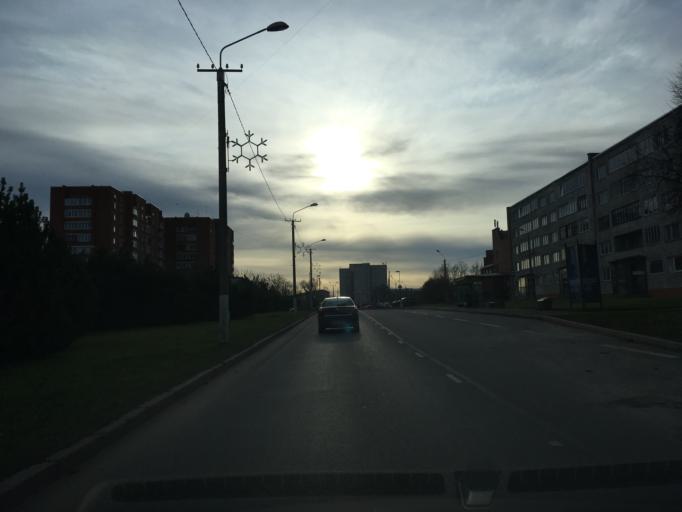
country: EE
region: Ida-Virumaa
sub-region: Narva linn
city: Narva
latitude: 59.3820
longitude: 28.1795
